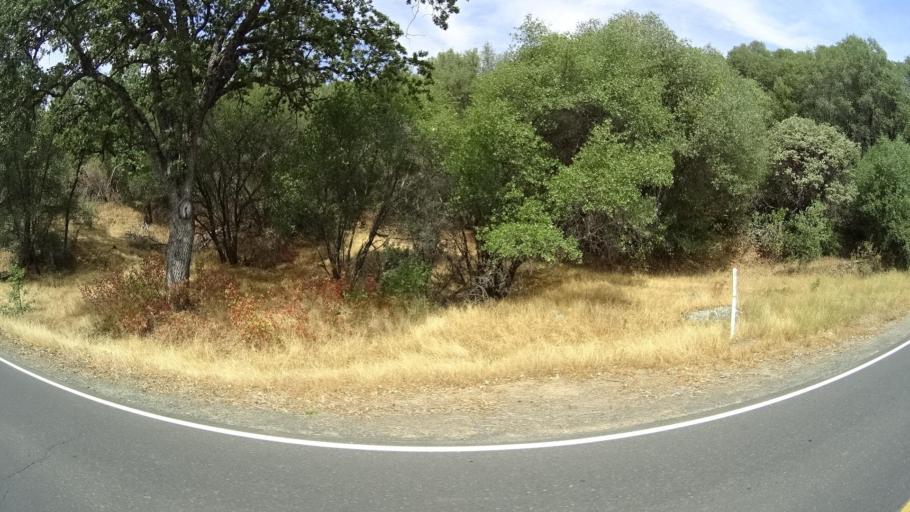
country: US
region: California
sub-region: Mariposa County
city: Midpines
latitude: 37.4904
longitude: -119.8574
